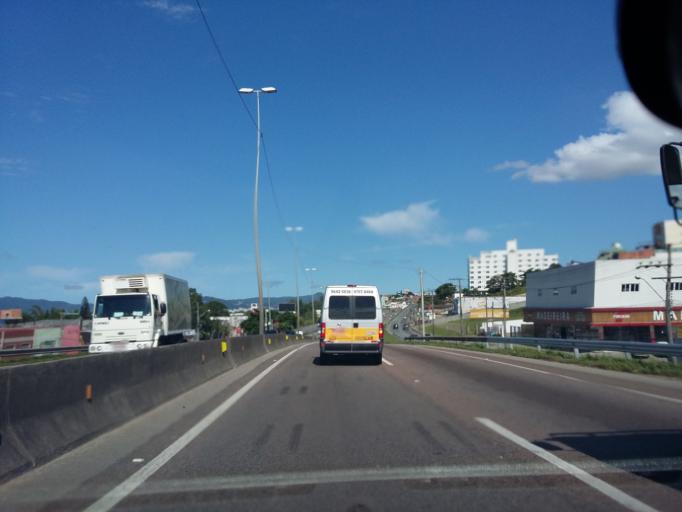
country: BR
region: Santa Catarina
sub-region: Biguacu
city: Biguacu
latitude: -27.5380
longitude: -48.6252
